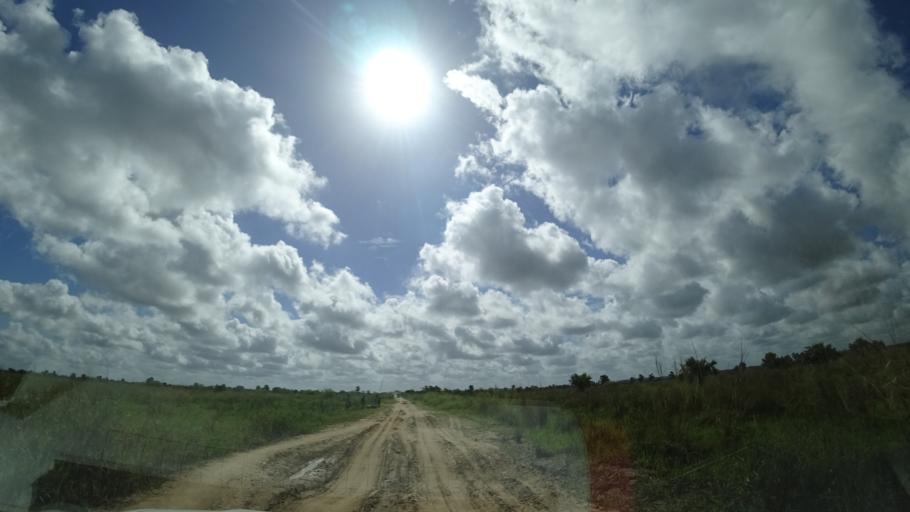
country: MZ
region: Sofala
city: Dondo
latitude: -19.3916
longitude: 34.5763
